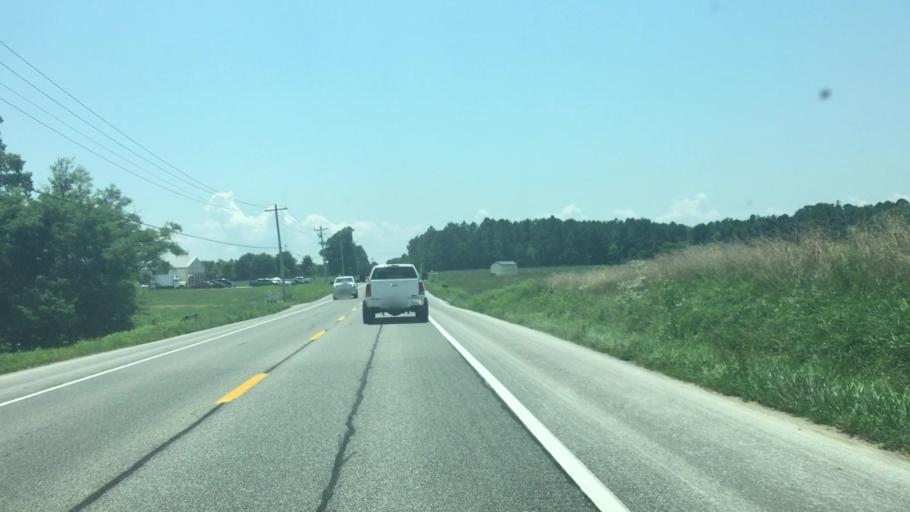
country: US
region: Maryland
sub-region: Saint Mary's County
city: Mechanicsville
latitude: 38.3762
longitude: -76.6780
